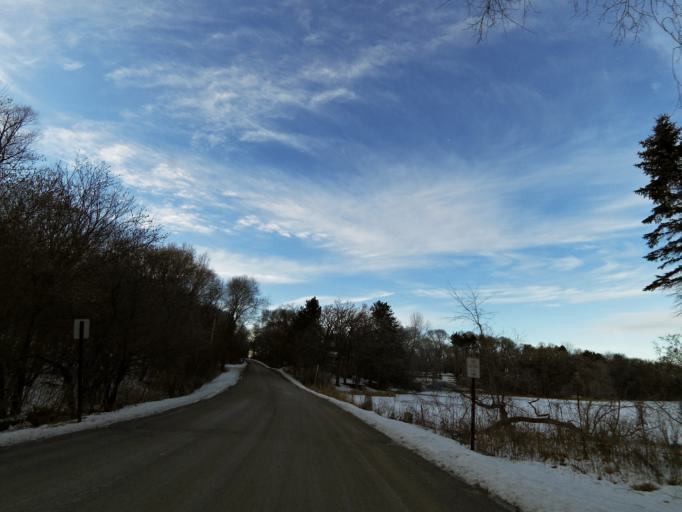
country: US
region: Minnesota
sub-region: Washington County
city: Afton
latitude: 44.9327
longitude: -92.8082
